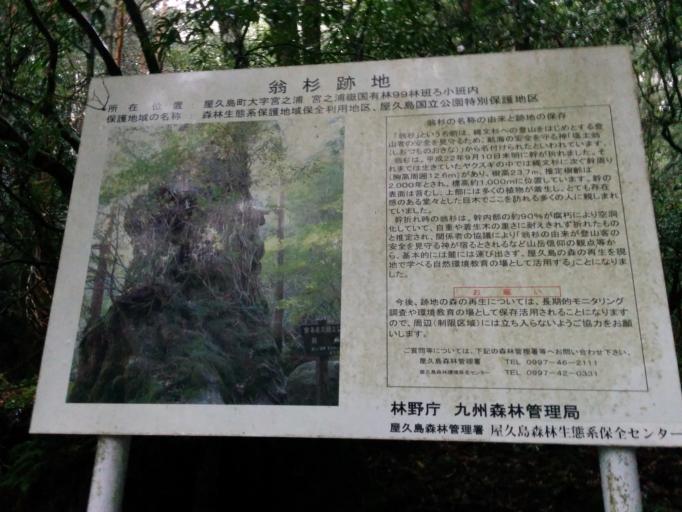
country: JP
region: Kagoshima
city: Nishinoomote
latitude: 30.3553
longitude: 130.5415
